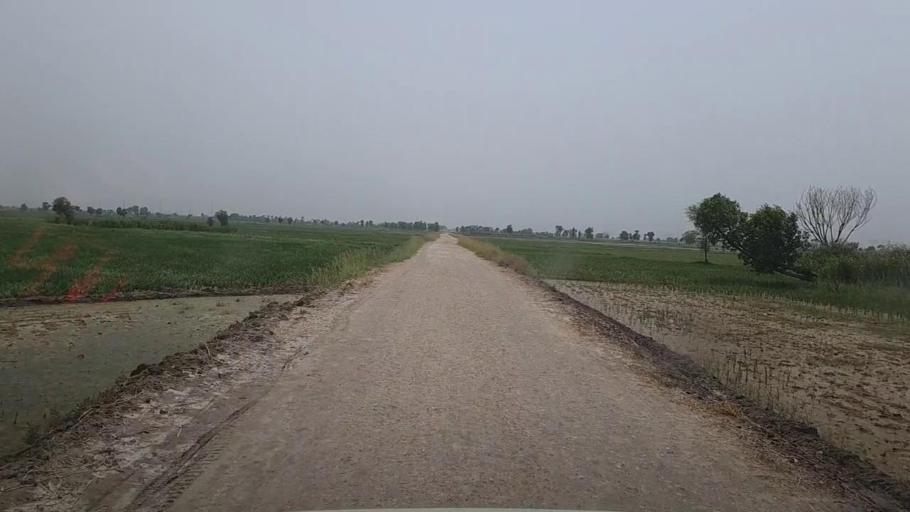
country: PK
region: Sindh
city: Sita Road
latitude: 27.0624
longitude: 67.8577
